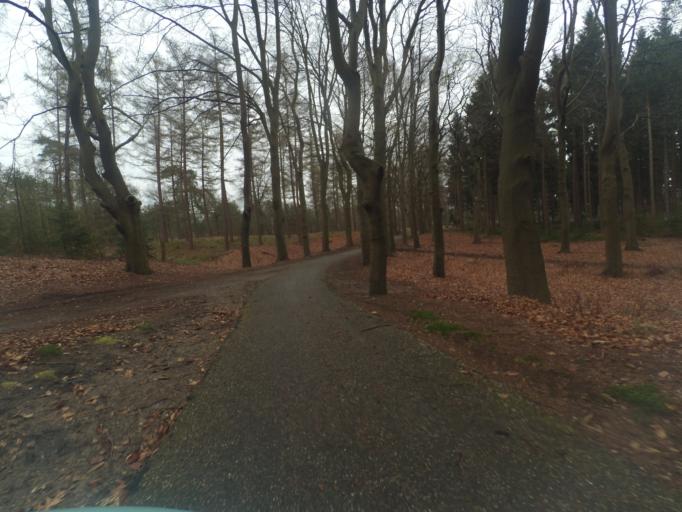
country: NL
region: Gelderland
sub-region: Gemeente Arnhem
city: Gulden Bodem
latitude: 52.0194
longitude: 5.9168
